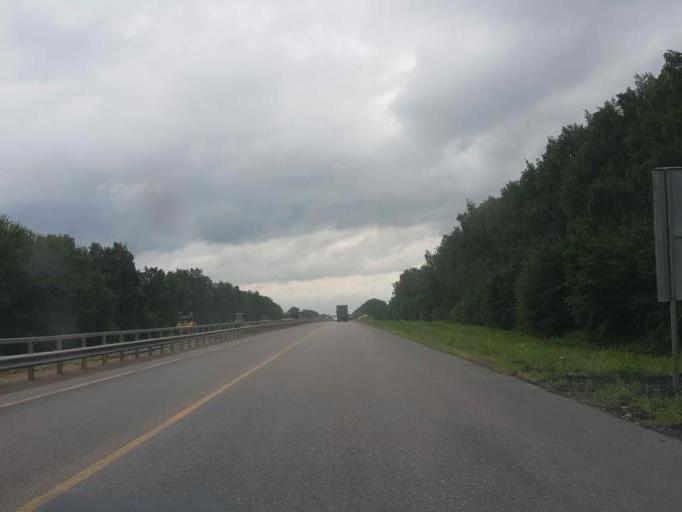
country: RU
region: Tambov
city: Selezni
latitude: 52.8064
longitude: 40.9672
